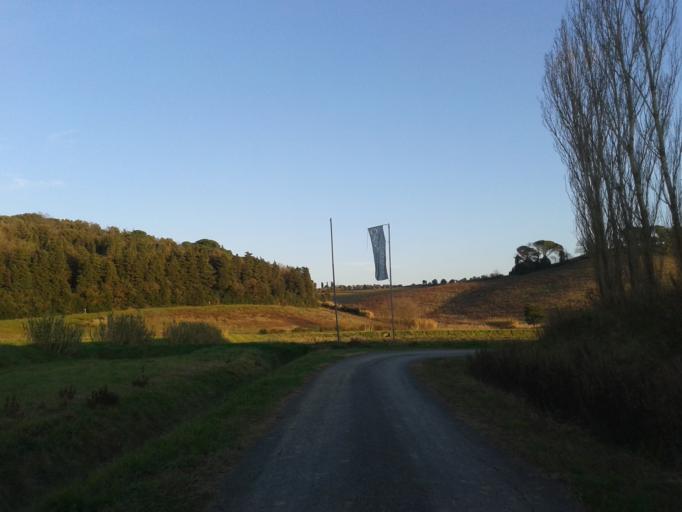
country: IT
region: Tuscany
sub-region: Provincia di Livorno
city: Guasticce
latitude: 43.5918
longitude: 10.4105
